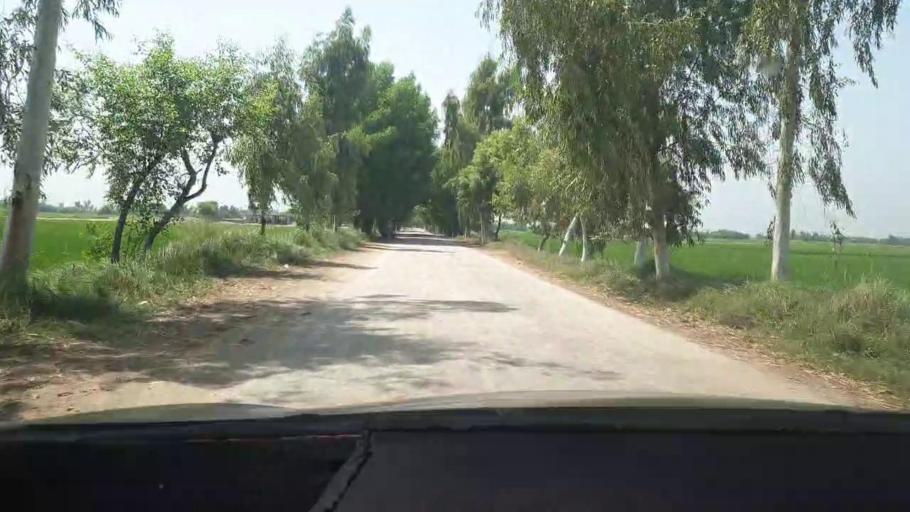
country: PK
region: Sindh
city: Miro Khan
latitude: 27.6718
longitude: 68.0580
